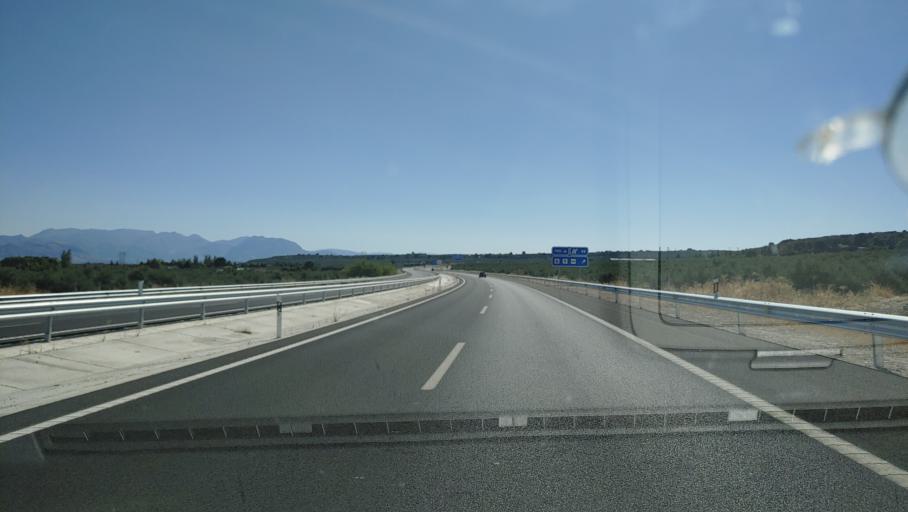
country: ES
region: Andalusia
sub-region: Provincia de Jaen
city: Sabiote
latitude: 38.0406
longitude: -3.3212
